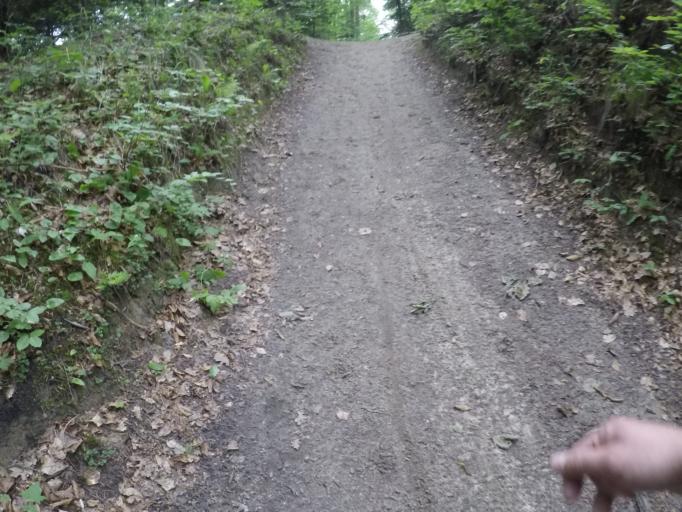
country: PL
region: Swietokrzyskie
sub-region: Powiat kielecki
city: Kielce
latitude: 50.8382
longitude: 20.6059
